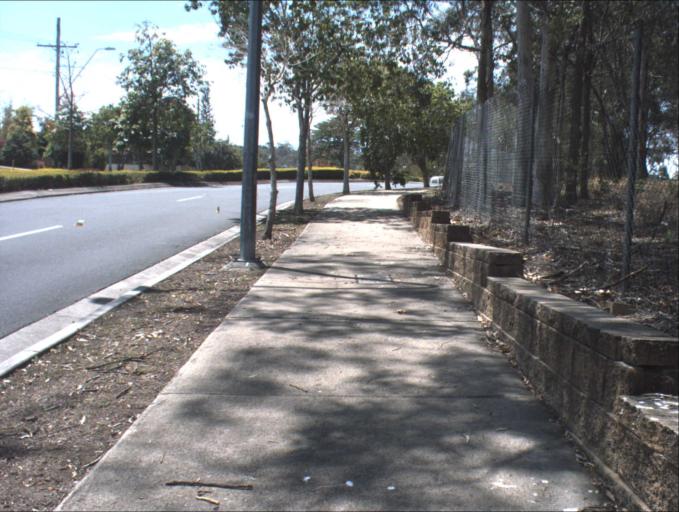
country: AU
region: Queensland
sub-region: Logan
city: Slacks Creek
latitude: -27.6375
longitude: 153.1474
